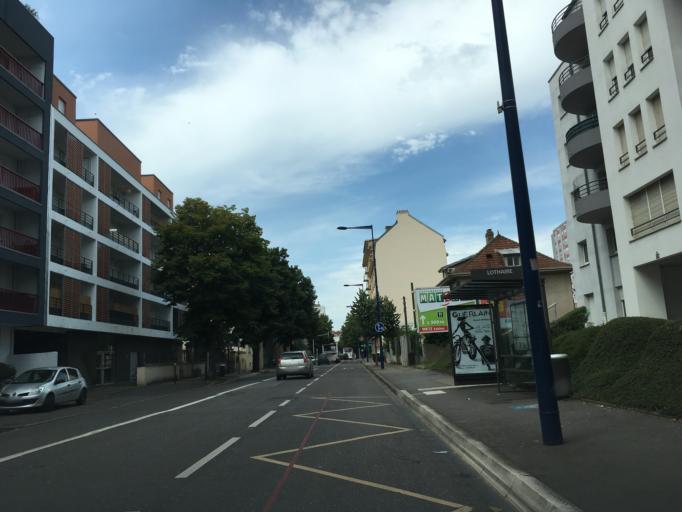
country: FR
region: Lorraine
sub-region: Departement de la Moselle
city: Metz
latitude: 49.0991
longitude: 6.1805
